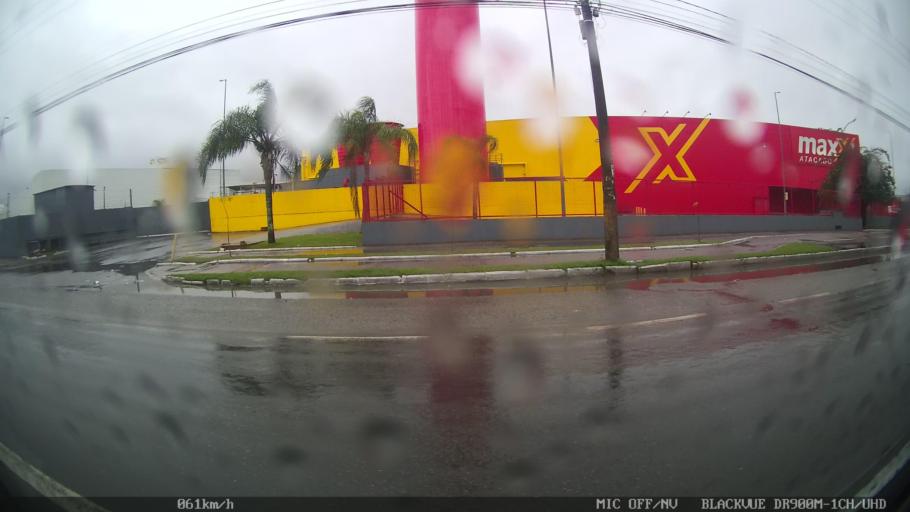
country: BR
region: Santa Catarina
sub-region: Itajai
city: Itajai
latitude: -26.9129
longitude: -48.6922
